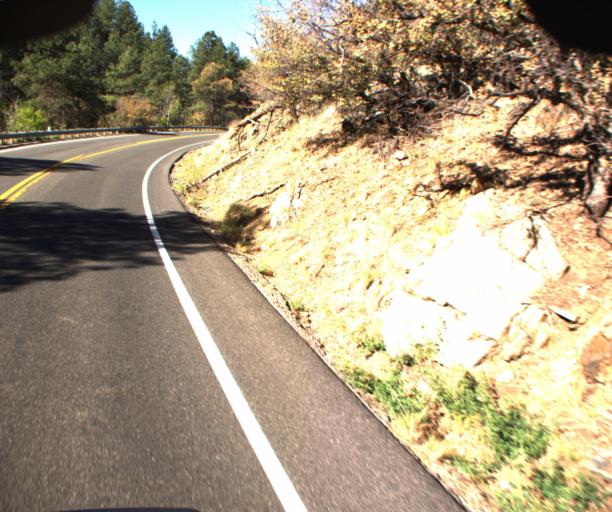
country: US
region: Arizona
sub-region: Yavapai County
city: Prescott
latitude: 34.4984
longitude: -112.4825
